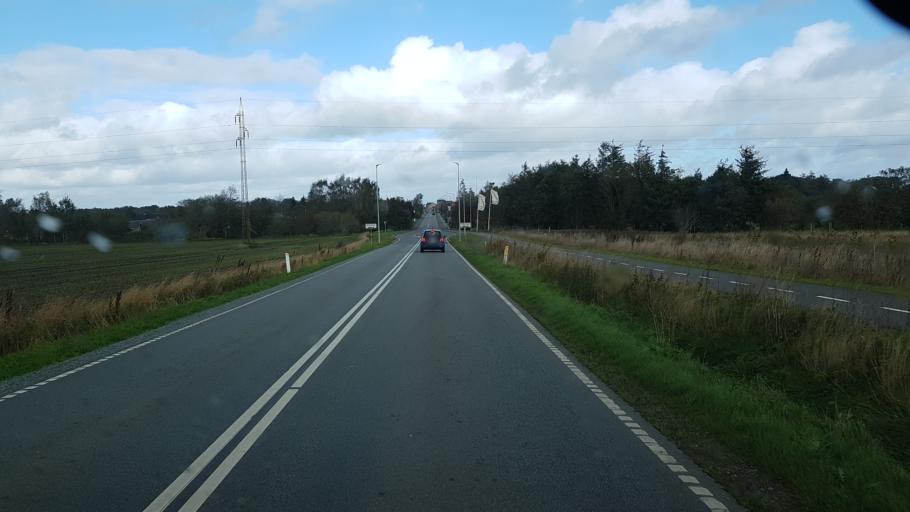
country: DK
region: South Denmark
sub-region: Vejen Kommune
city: Holsted
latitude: 55.4772
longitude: 8.9081
